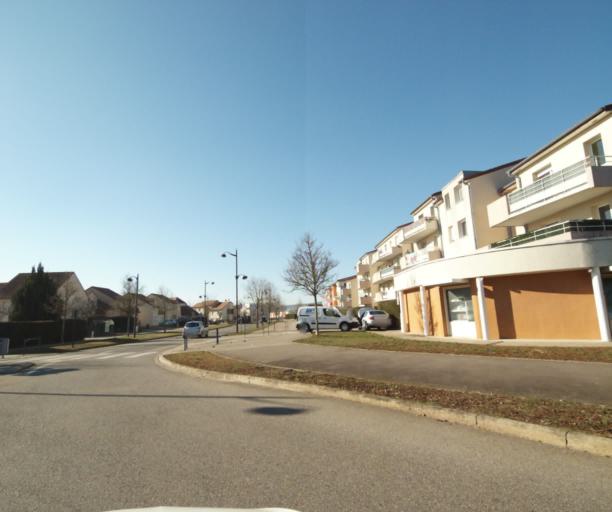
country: FR
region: Lorraine
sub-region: Departement de Meurthe-et-Moselle
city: Pulnoy
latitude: 48.6989
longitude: 6.2544
